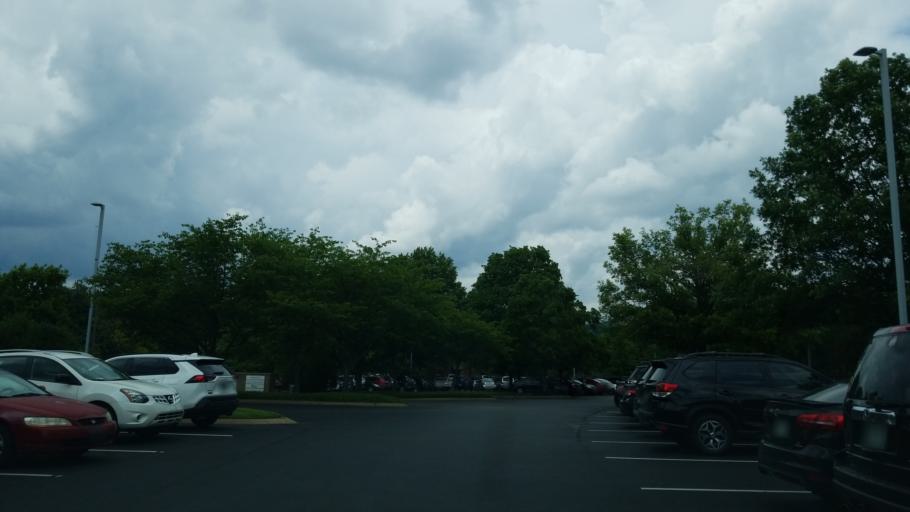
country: US
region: Tennessee
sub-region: Williamson County
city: Brentwood
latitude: 36.0329
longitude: -86.8062
